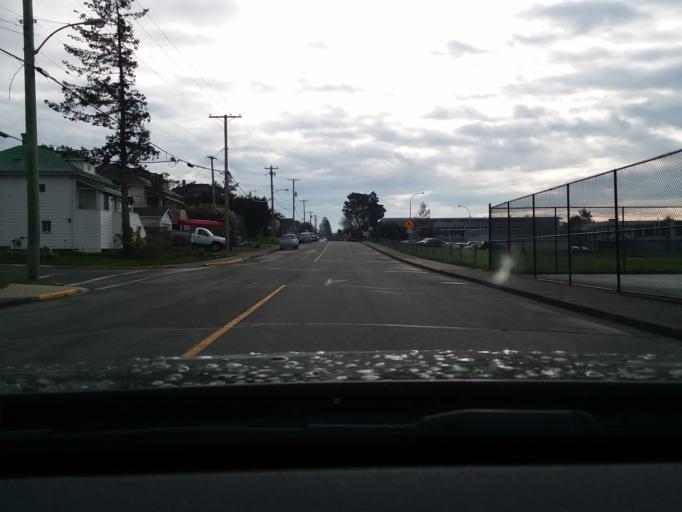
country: CA
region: British Columbia
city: Victoria
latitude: 48.4388
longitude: -123.3994
